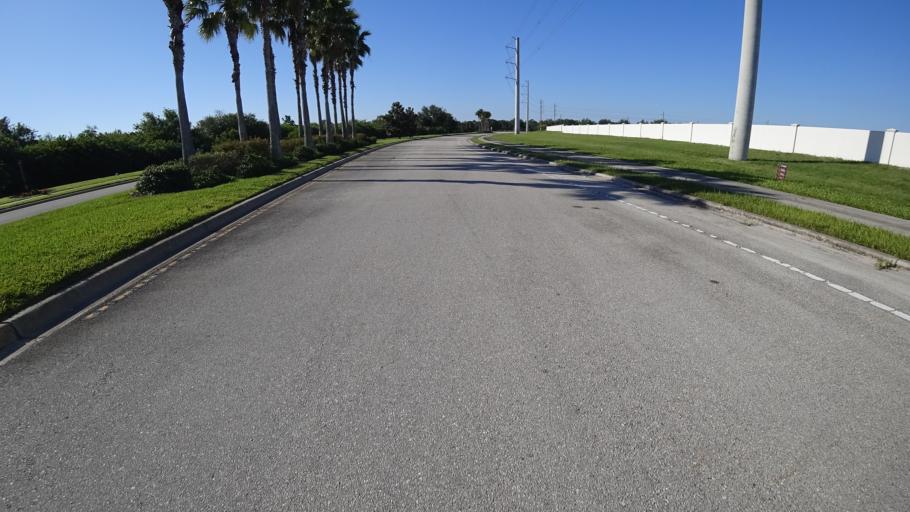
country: US
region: Florida
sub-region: Sarasota County
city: The Meadows
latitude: 27.3889
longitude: -82.3531
